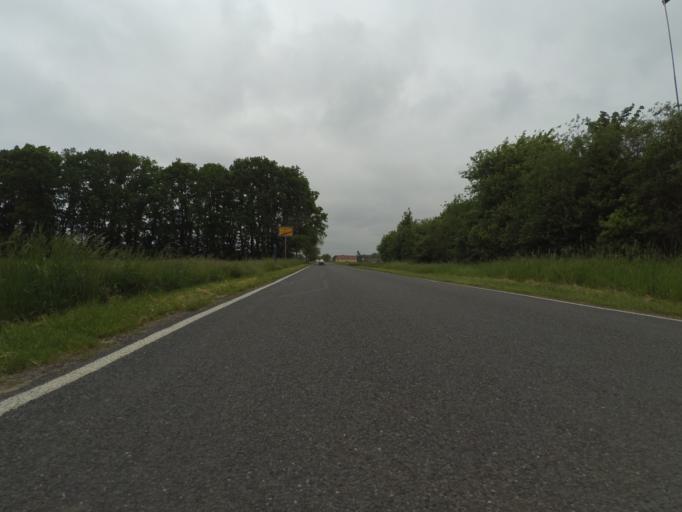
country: DE
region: Lower Saxony
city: Edemissen
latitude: 52.3941
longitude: 10.3215
